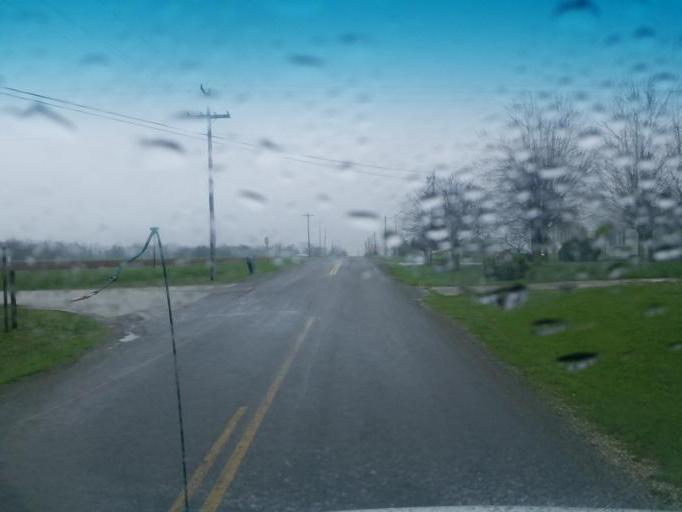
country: US
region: Ohio
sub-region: Wyandot County
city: Carey
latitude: 40.9922
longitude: -83.3870
